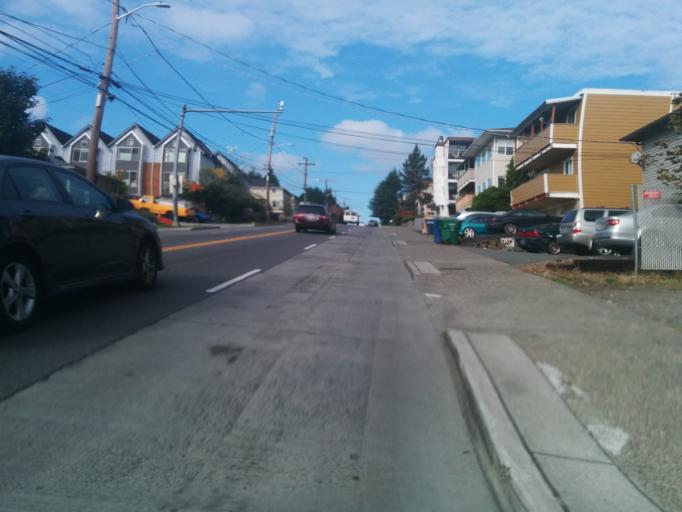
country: US
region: Washington
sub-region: King County
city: Shoreline
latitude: 47.6905
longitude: -122.3458
